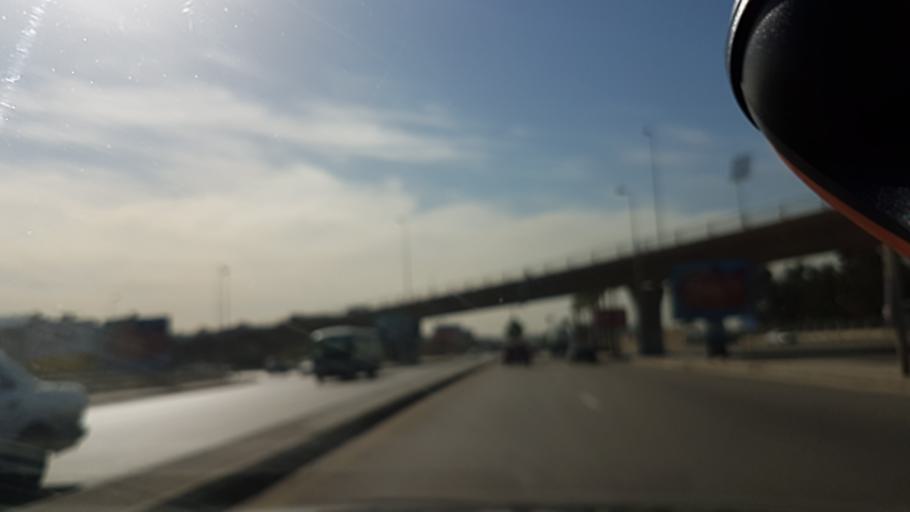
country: LB
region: Liban-Sud
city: Sidon
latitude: 33.5880
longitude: 35.3868
